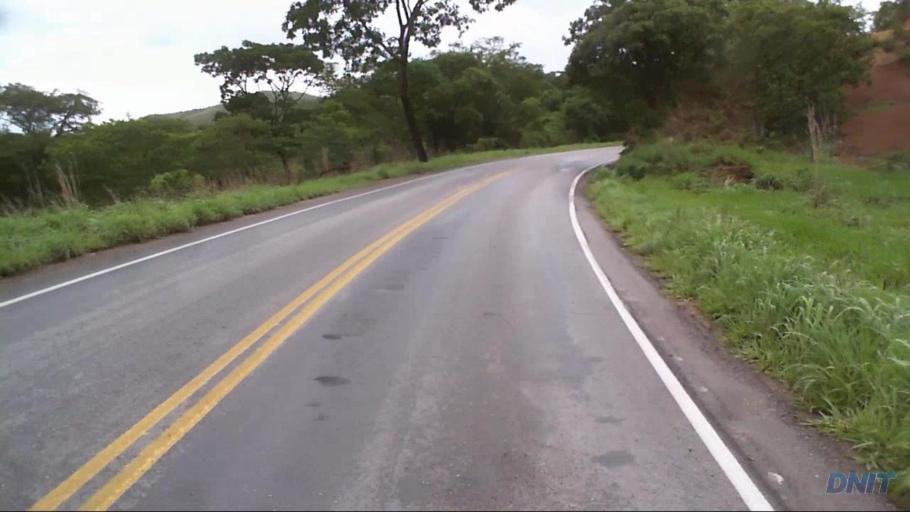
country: BR
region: Goias
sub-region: Padre Bernardo
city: Padre Bernardo
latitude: -15.4941
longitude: -48.2236
